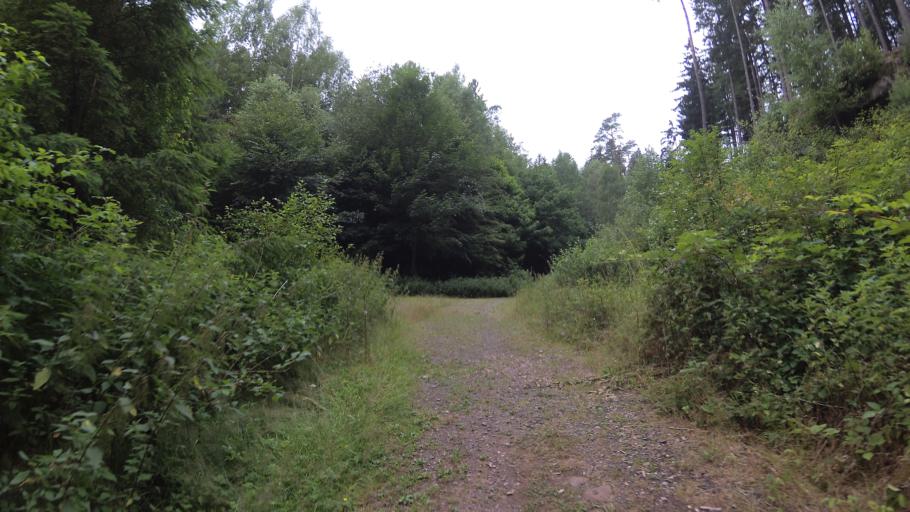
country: DE
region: Rheinland-Pfalz
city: Bechhofen
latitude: 49.3178
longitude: 7.3773
